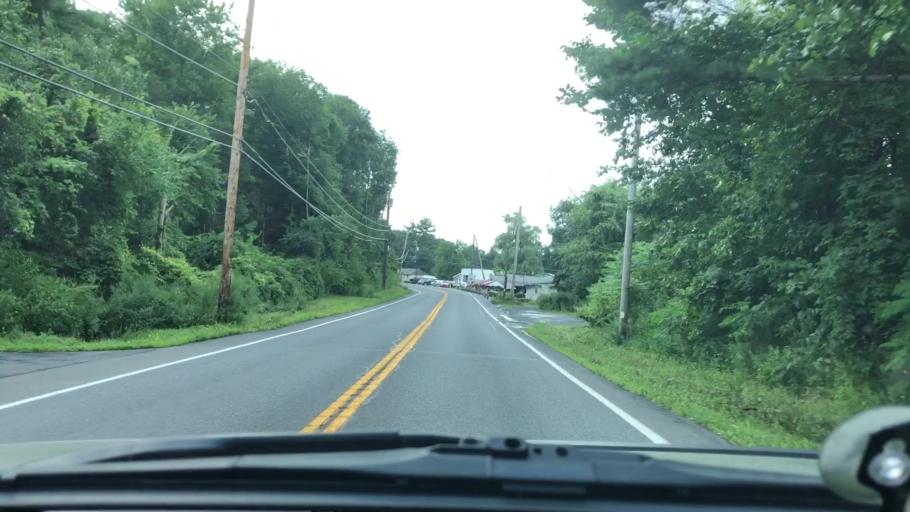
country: US
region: New York
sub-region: Ulster County
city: Manorville
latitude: 42.1371
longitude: -74.0013
